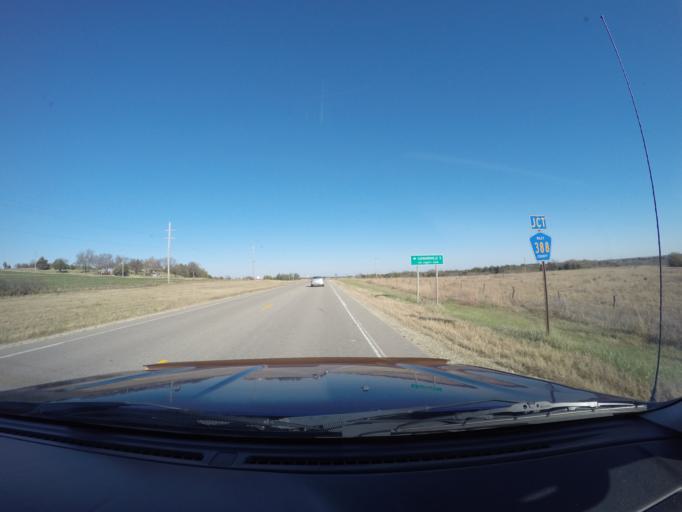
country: US
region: Kansas
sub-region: Riley County
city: Ogden
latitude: 39.3624
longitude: -96.7563
